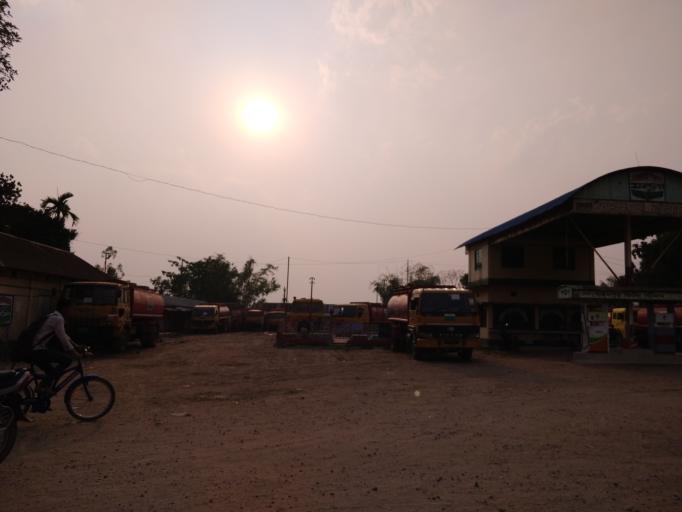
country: IN
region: Tripura
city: Khowai
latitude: 24.1321
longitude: 91.3521
